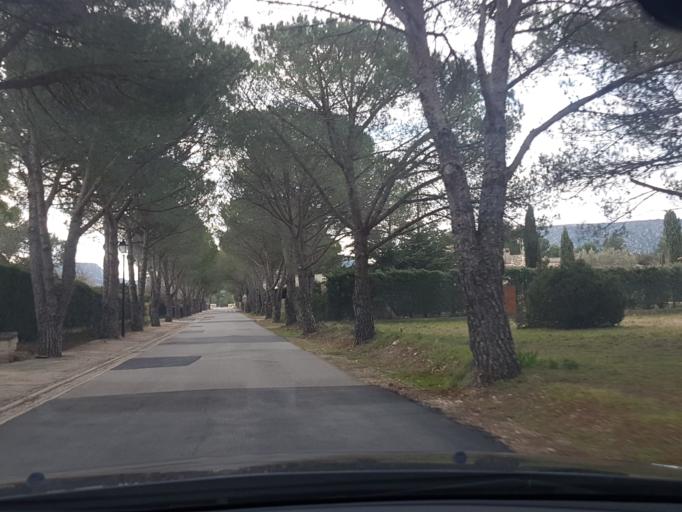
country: FR
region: Provence-Alpes-Cote d'Azur
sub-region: Departement des Bouches-du-Rhone
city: Eygalieres
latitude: 43.7565
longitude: 4.9518
